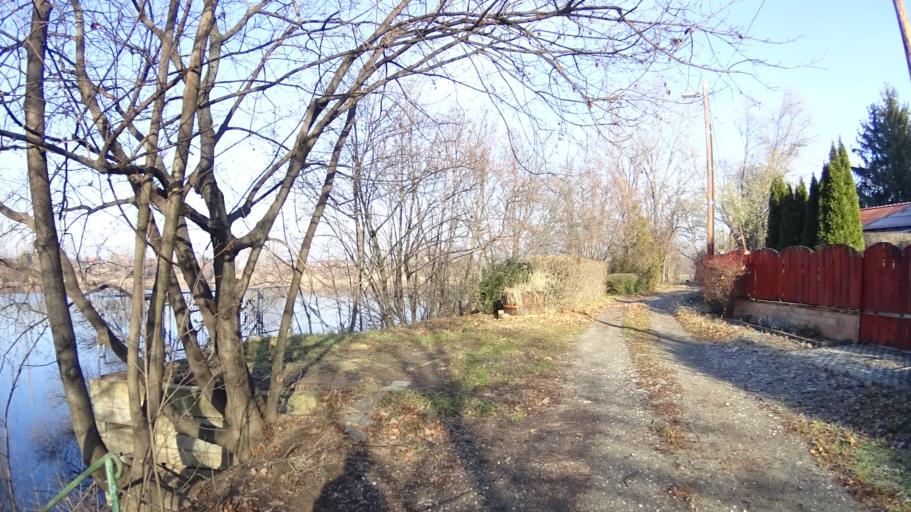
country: HU
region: Borsod-Abauj-Zemplen
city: Nyekladhaza
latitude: 47.9882
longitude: 20.8544
